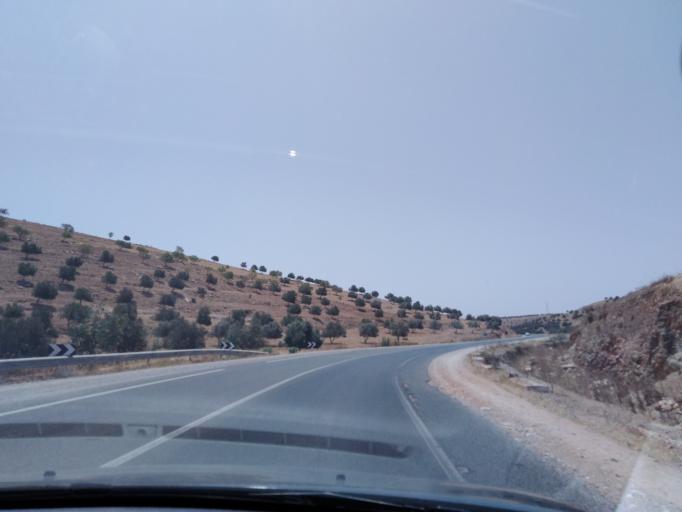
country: MA
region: Doukkala-Abda
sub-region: Safi
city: Youssoufia
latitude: 32.1500
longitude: -8.8419
